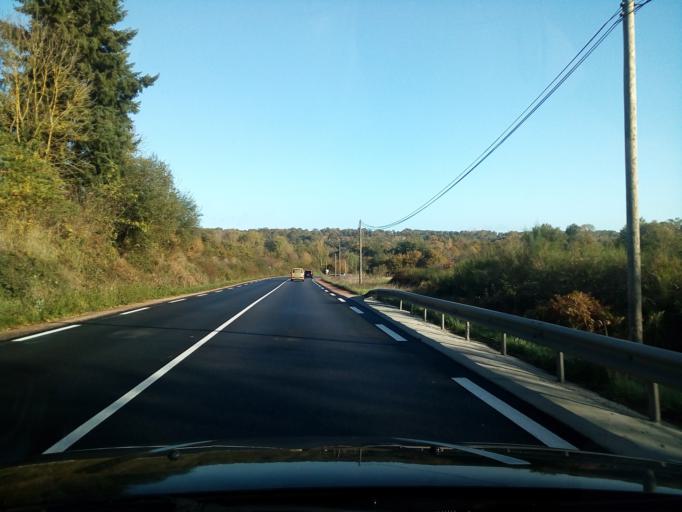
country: FR
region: Limousin
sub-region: Departement de la Haute-Vienne
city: Bellac
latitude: 46.1479
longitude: 1.1036
